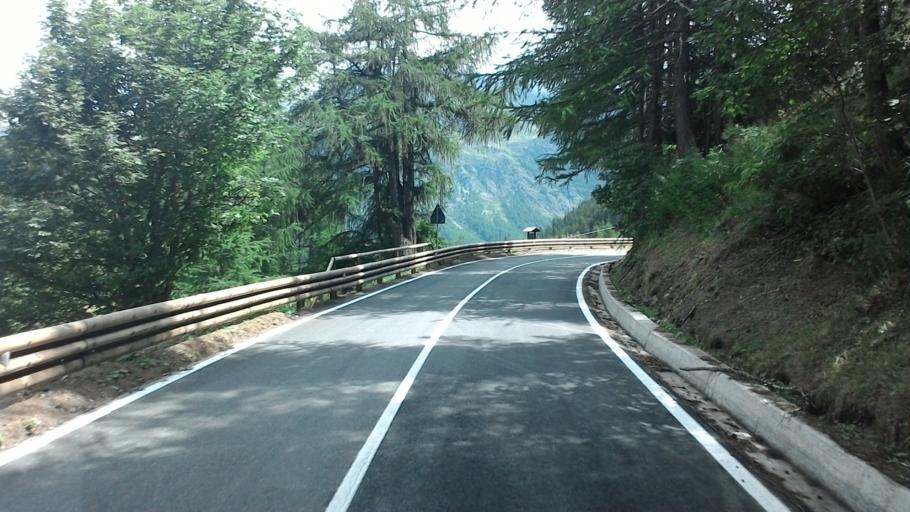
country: IT
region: Aosta Valley
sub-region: Valle d'Aosta
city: La Thuile
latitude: 45.7105
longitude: 6.9316
